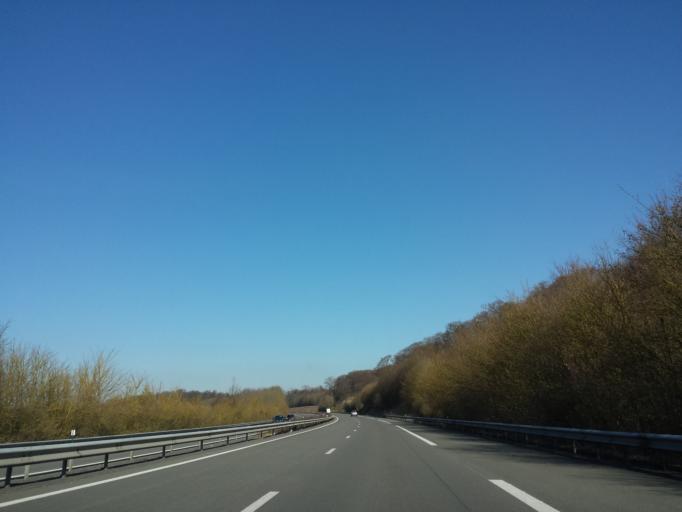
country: FR
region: Picardie
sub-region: Departement de l'Oise
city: Breteuil
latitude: 49.6458
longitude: 2.2163
